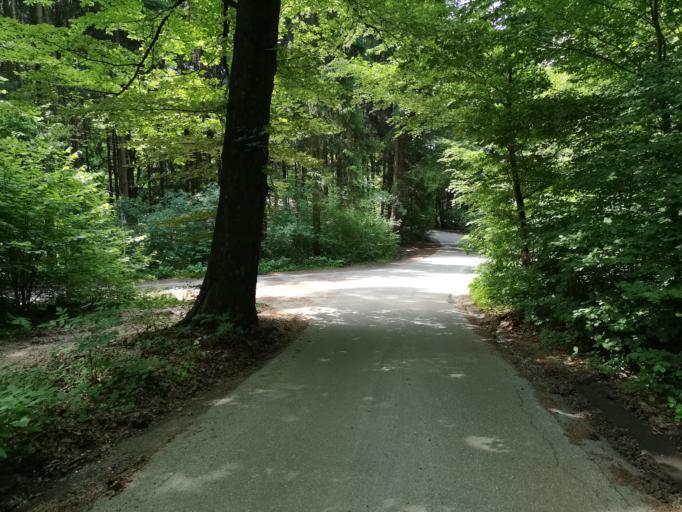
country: AT
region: Styria
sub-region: Graz Stadt
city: Wetzelsdorf
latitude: 47.0329
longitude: 15.3700
